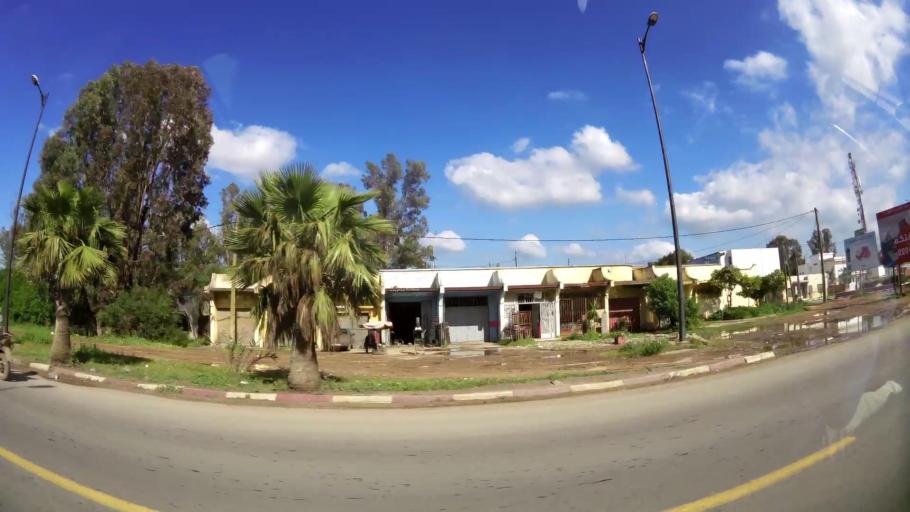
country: MA
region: Grand Casablanca
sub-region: Mediouna
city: Mediouna
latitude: 33.3762
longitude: -7.5412
